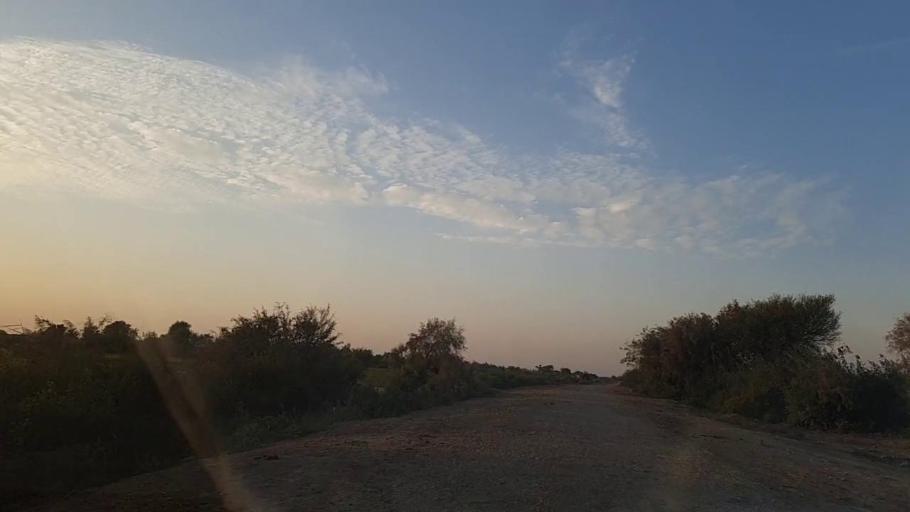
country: PK
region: Sindh
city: Chuhar Jamali
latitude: 24.4577
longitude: 68.1154
